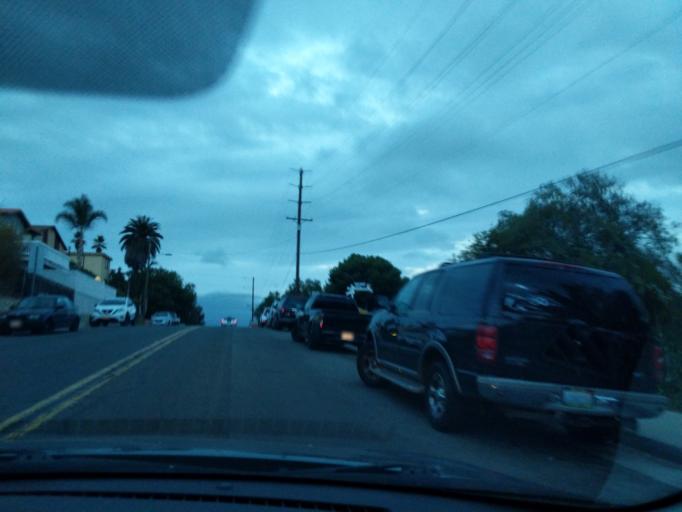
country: US
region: California
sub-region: San Diego County
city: San Diego
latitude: 32.7170
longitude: -117.1227
